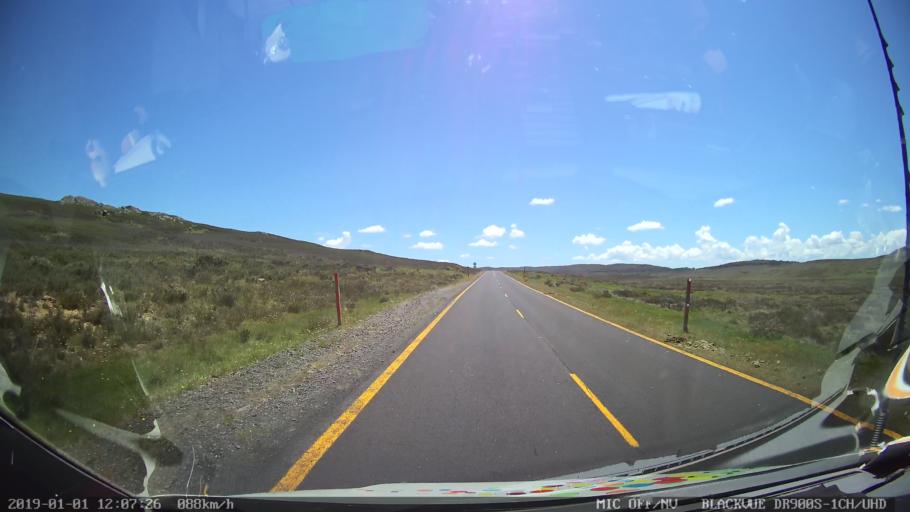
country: AU
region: New South Wales
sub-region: Tumut Shire
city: Tumut
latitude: -35.8329
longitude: 148.4897
